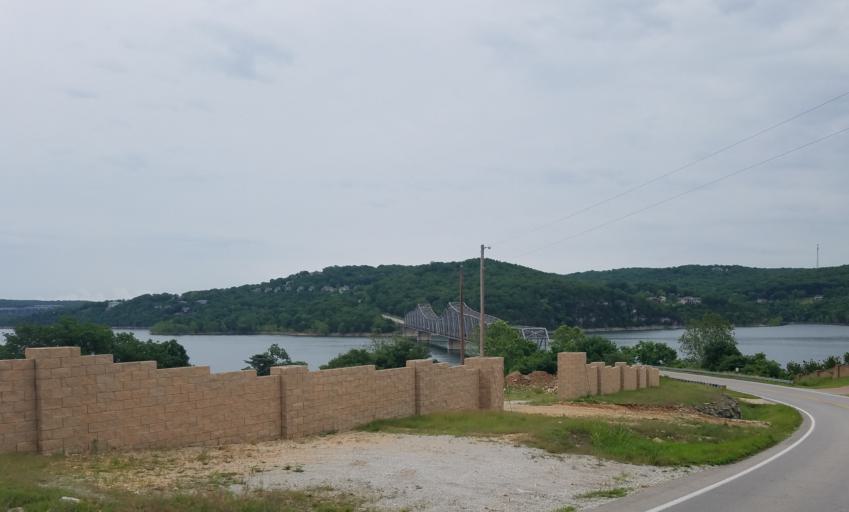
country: US
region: Missouri
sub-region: Taney County
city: Hollister
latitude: 36.5272
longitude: -93.3086
